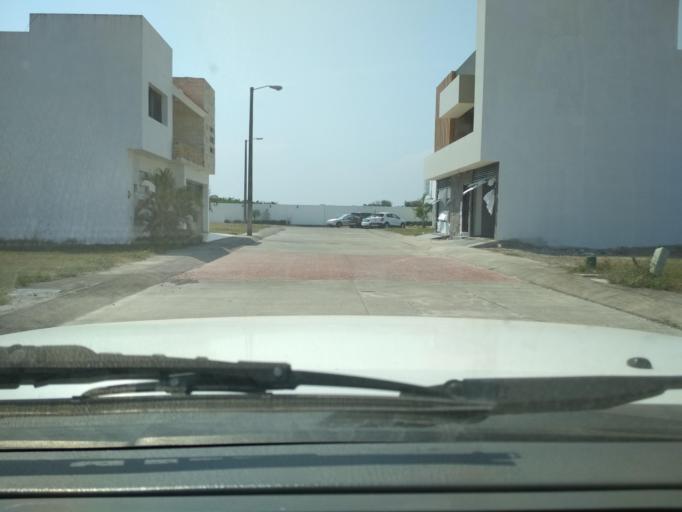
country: MX
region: Veracruz
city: Boca del Rio
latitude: 19.1037
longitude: -96.1254
